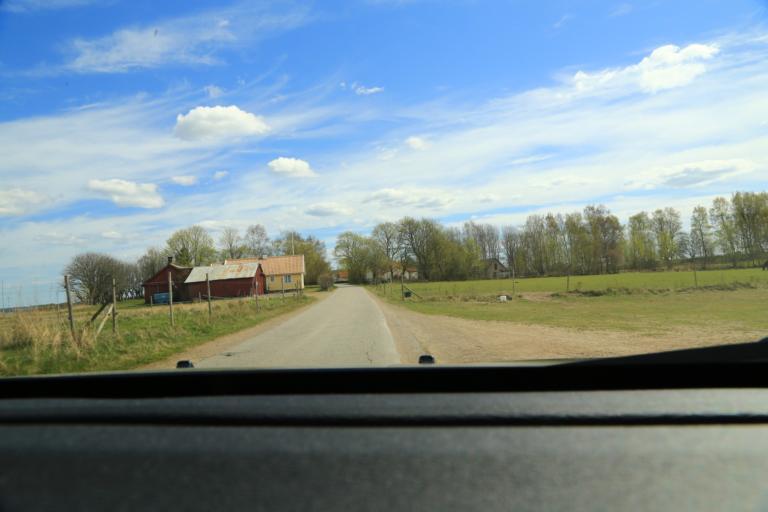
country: SE
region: Halland
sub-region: Varbergs Kommun
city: Traslovslage
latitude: 57.1175
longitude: 12.3127
